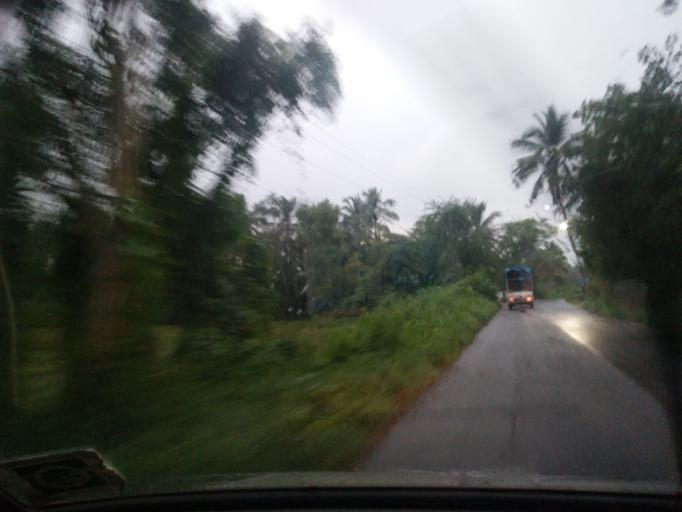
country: IN
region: Goa
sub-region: South Goa
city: Madgaon
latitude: 15.2877
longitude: 73.9471
